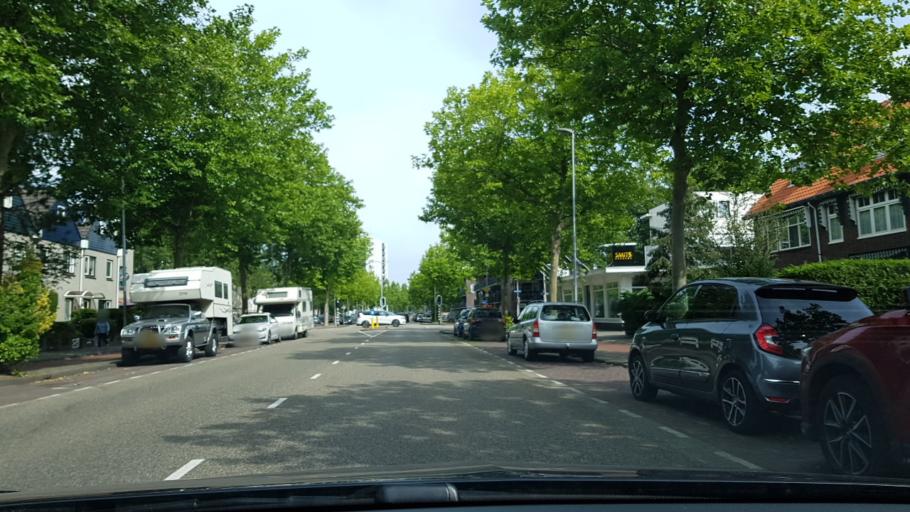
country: NL
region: North Holland
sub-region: Gemeente Bloemendaal
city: Bloemendaal
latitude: 52.4186
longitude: 4.6485
